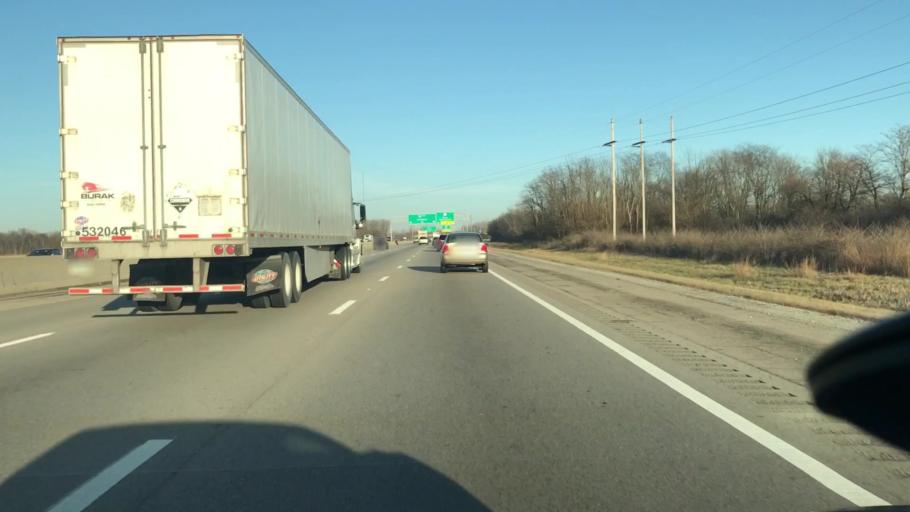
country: US
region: Ohio
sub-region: Clark County
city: Green Meadows
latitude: 39.8790
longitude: -83.9599
